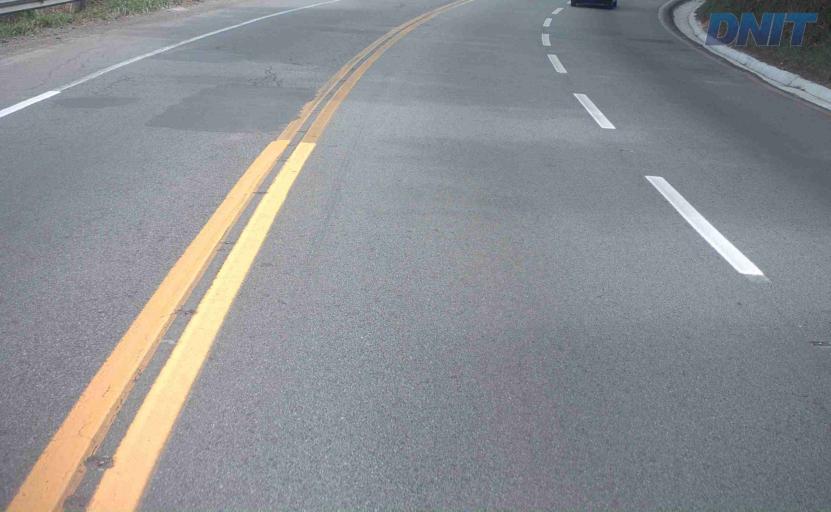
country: BR
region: Minas Gerais
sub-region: Santa Luzia
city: Santa Luzia
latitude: -19.8006
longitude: -43.7507
